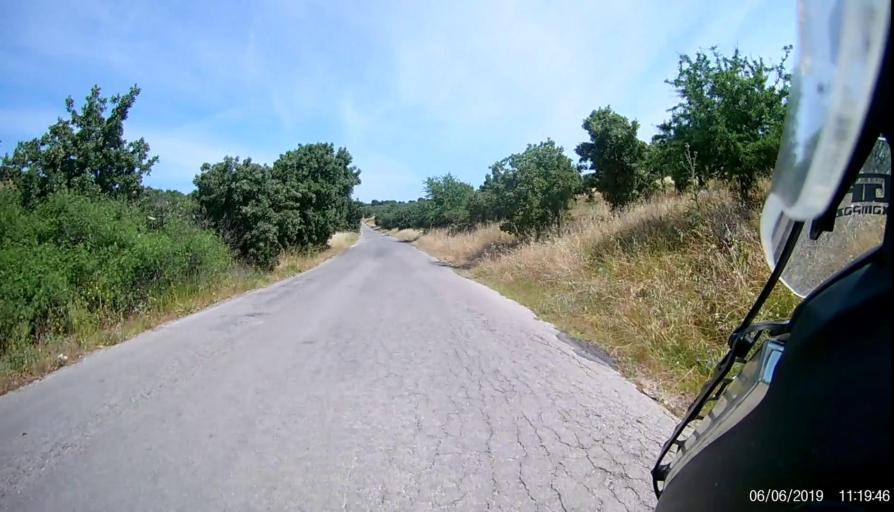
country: TR
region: Canakkale
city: Gulpinar
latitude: 39.6600
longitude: 26.1642
